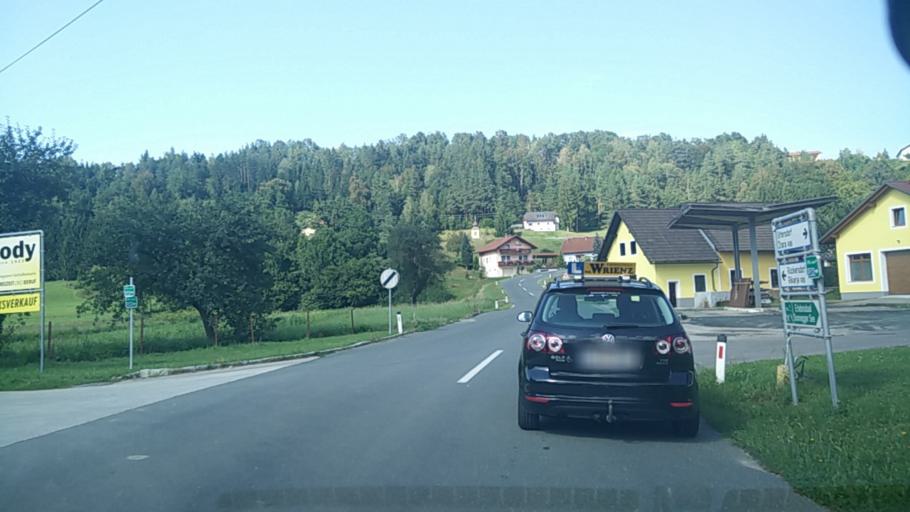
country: AT
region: Carinthia
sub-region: Politischer Bezirk Volkermarkt
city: Sittersdorf
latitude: 46.5583
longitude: 14.5635
